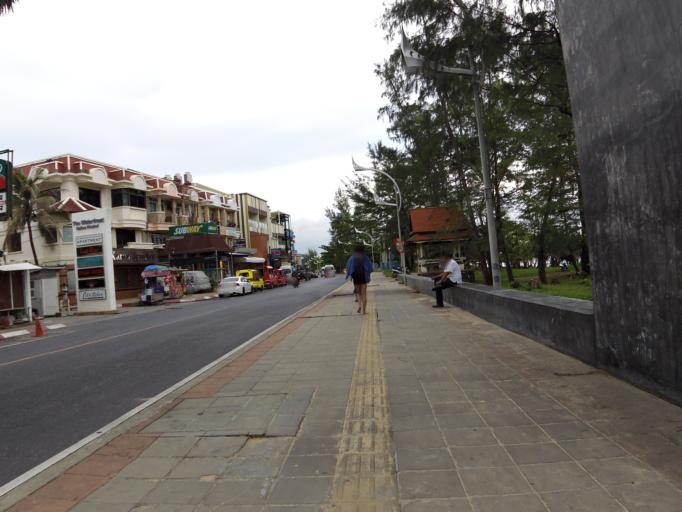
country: TH
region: Phuket
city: Ban Karon
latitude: 7.8481
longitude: 98.2933
